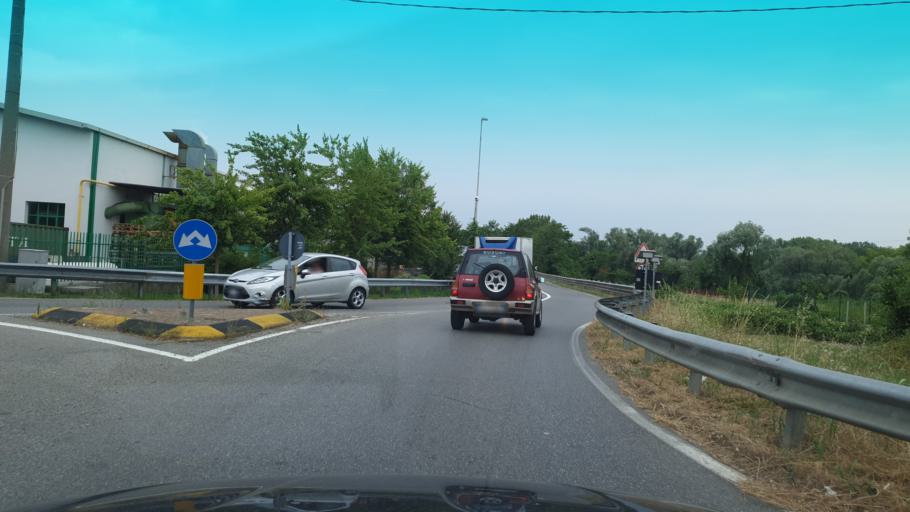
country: IT
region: Lombardy
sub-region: Provincia di Bergamo
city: Badalasco
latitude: 45.5374
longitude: 9.5372
